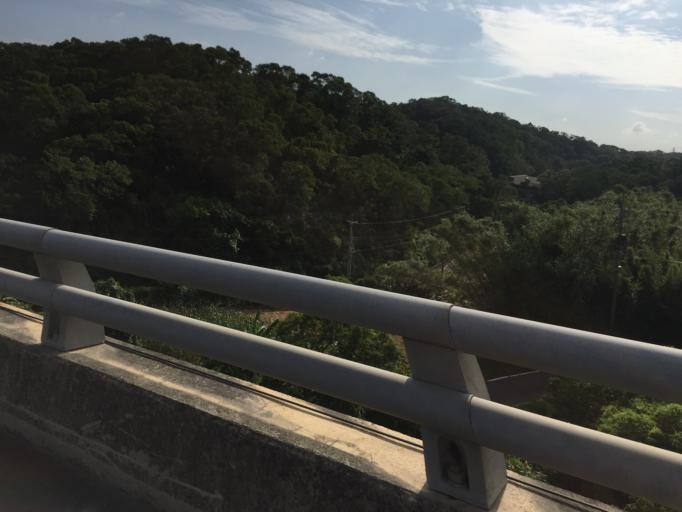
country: TW
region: Taiwan
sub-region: Hsinchu
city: Hsinchu
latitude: 24.7653
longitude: 120.9561
